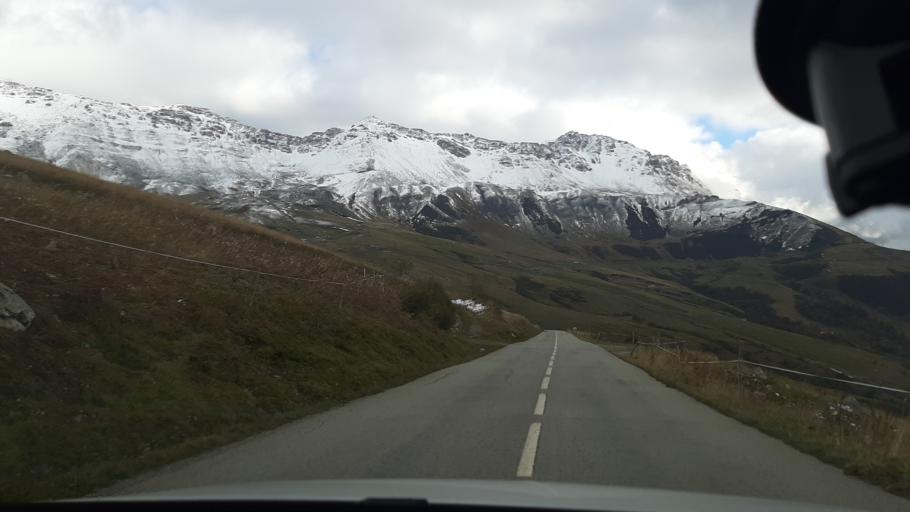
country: FR
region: Rhone-Alpes
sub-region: Departement de la Savoie
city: La Chambre
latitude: 45.4297
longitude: 6.3664
